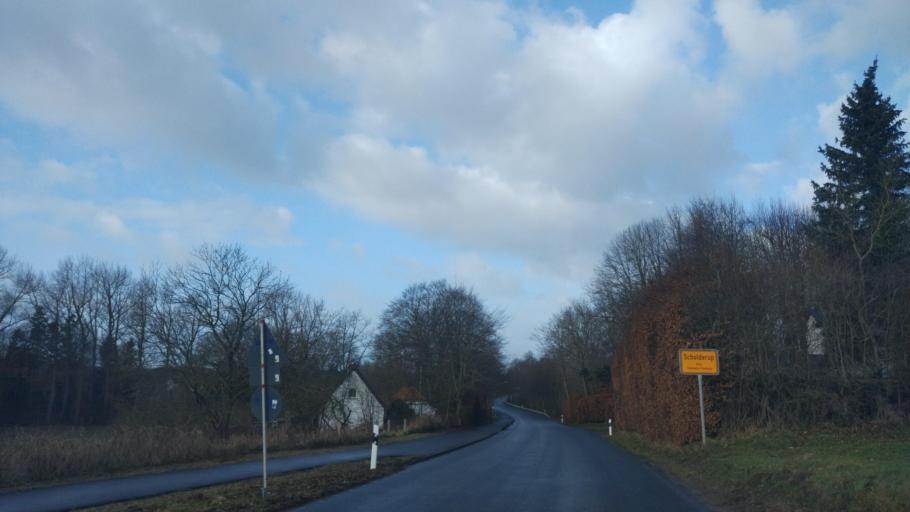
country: DE
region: Schleswig-Holstein
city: Taarstedt
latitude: 54.5624
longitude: 9.6828
